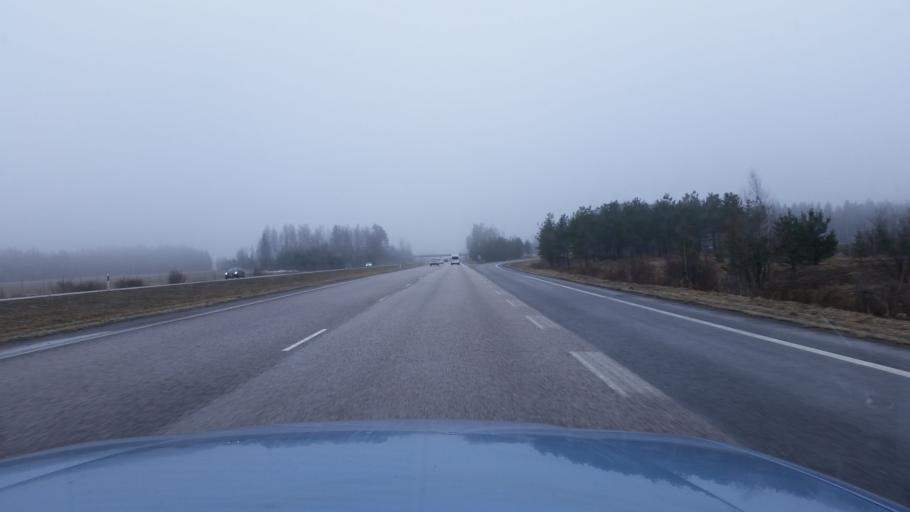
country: FI
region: Uusimaa
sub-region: Helsinki
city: Nurmijaervi
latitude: 60.5230
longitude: 24.8443
